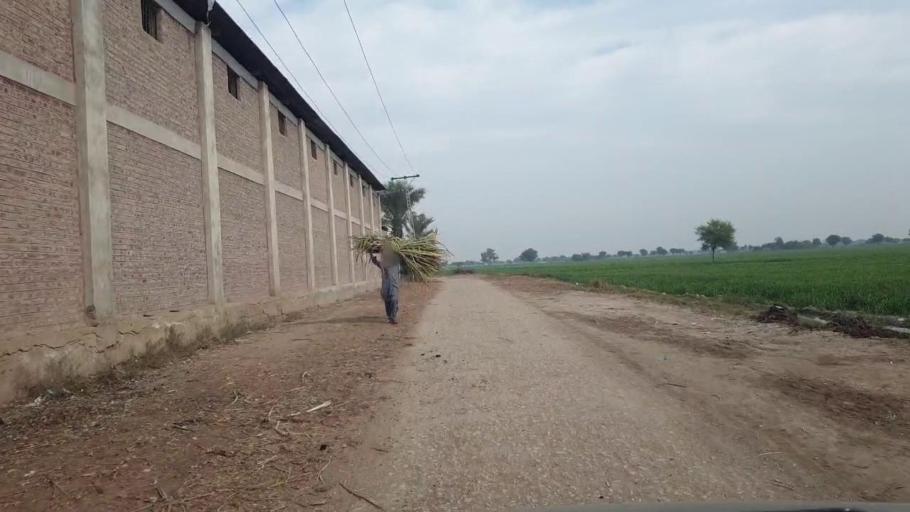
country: PK
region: Sindh
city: Shahdadpur
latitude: 25.9325
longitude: 68.6810
